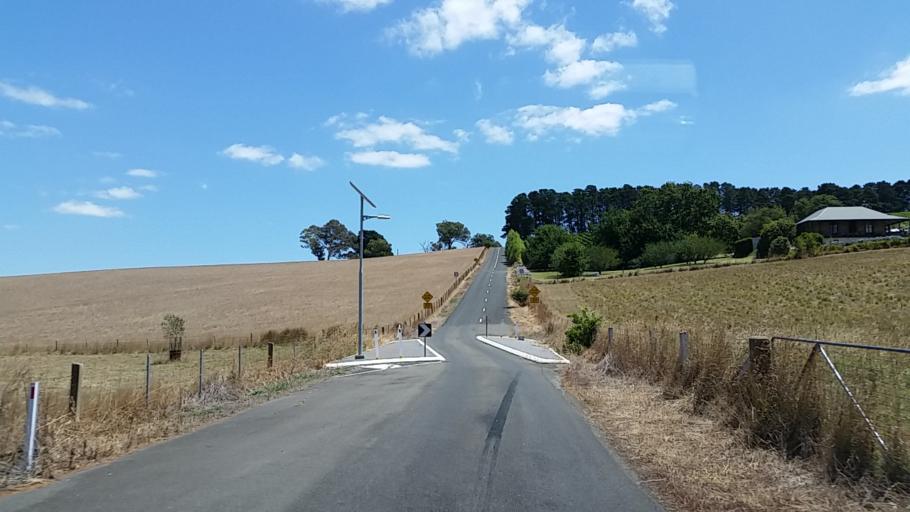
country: AU
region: South Australia
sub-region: Adelaide Hills
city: Lobethal
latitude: -34.9058
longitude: 138.8898
